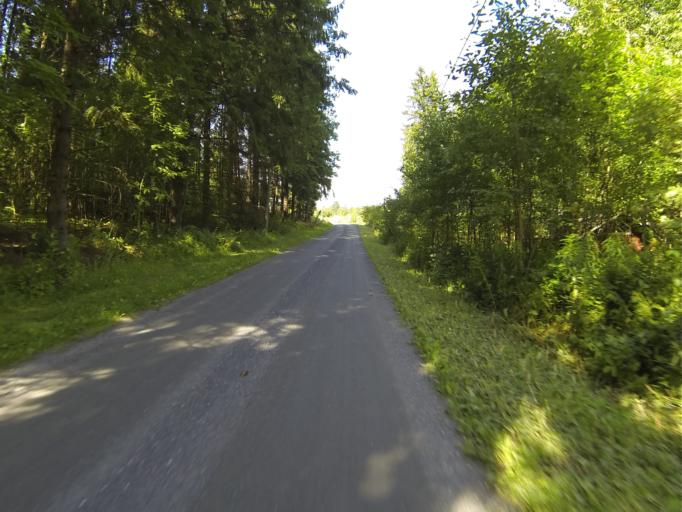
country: FI
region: Varsinais-Suomi
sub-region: Salo
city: Halikko
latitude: 60.2732
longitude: 22.9881
